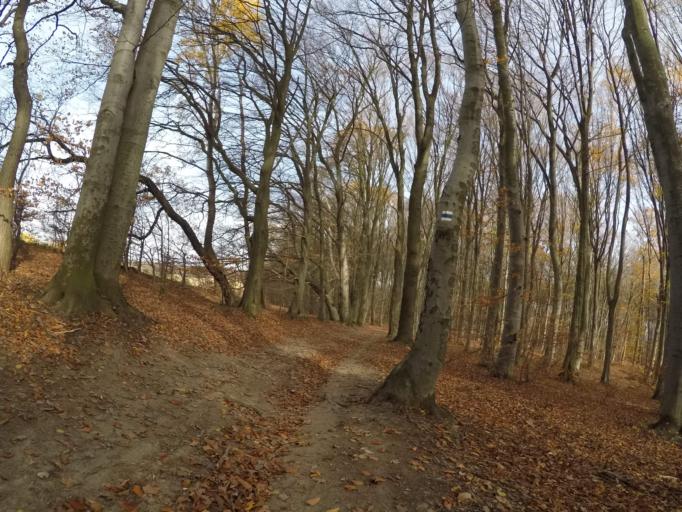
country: SK
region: Presovsky
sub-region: Okres Presov
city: Presov
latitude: 48.9176
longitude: 21.2193
